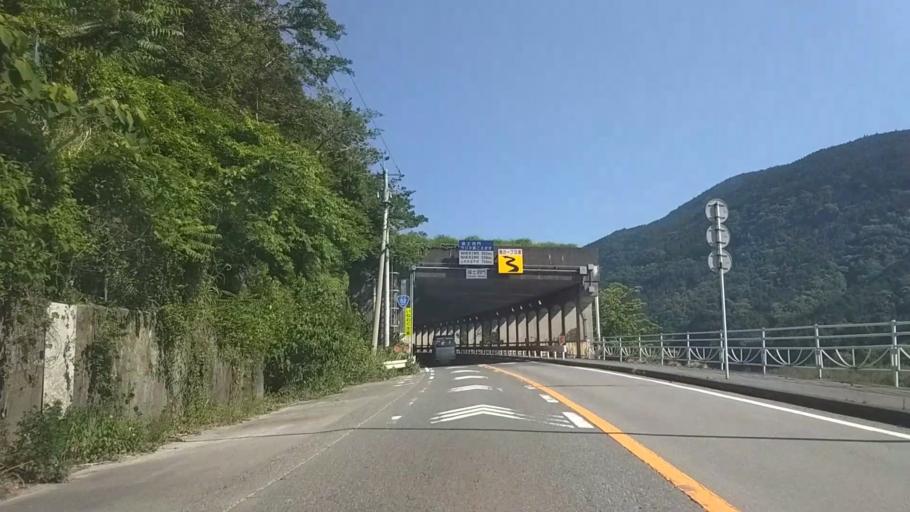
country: JP
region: Shizuoka
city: Fujinomiya
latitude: 35.2548
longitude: 138.4781
